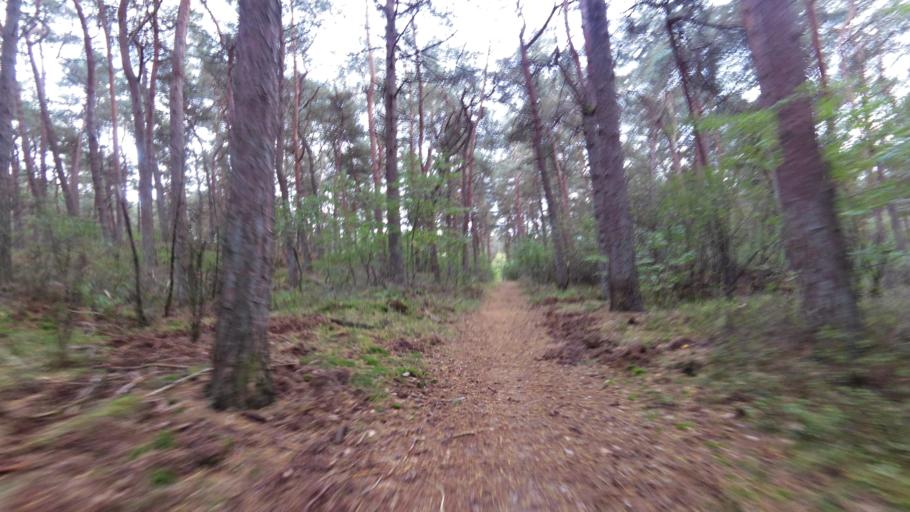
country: NL
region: Gelderland
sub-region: Gemeente Barneveld
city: Stroe
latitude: 52.1709
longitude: 5.7334
